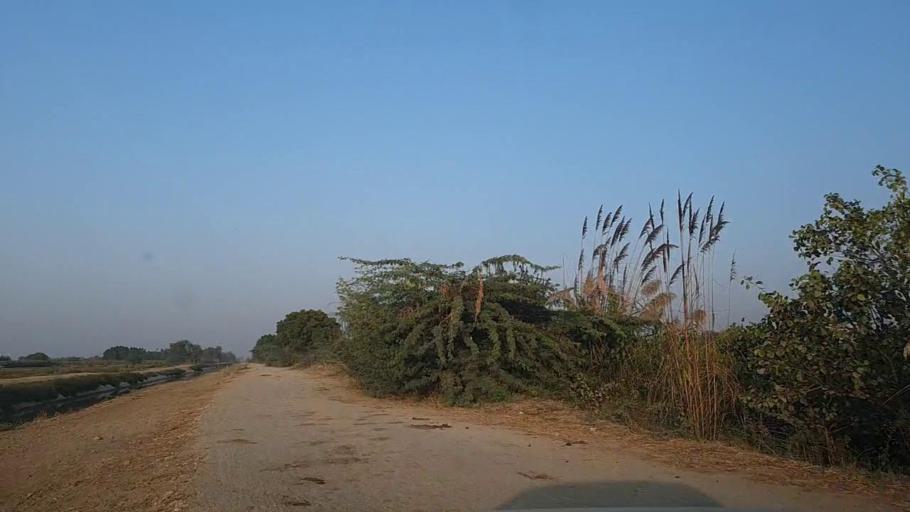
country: PK
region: Sindh
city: Mirpur Sakro
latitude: 24.2908
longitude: 67.6938
